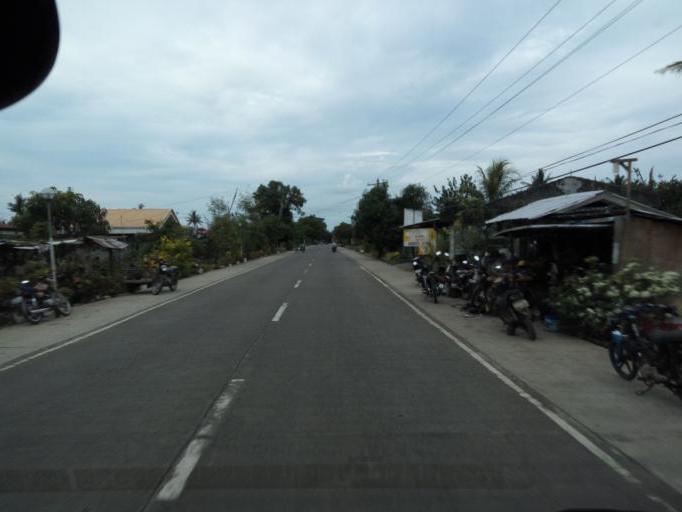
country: PH
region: Cagayan Valley
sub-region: Province of Cagayan
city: Tapel
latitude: 18.2796
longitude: 122.0094
